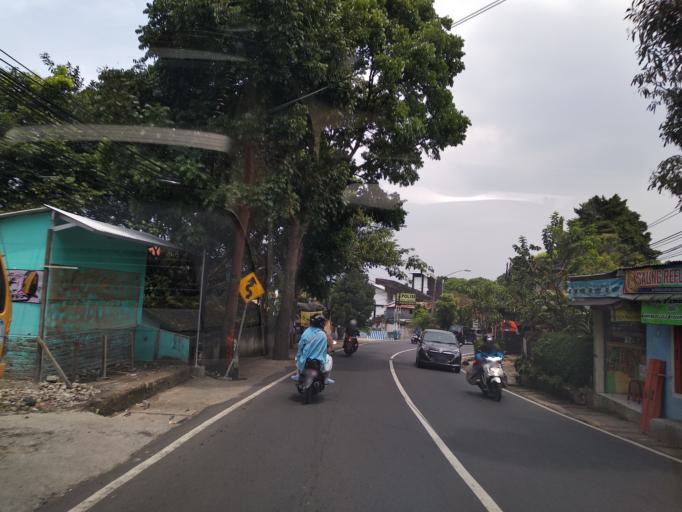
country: ID
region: West Java
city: Lembang
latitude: -6.8469
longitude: 107.5993
